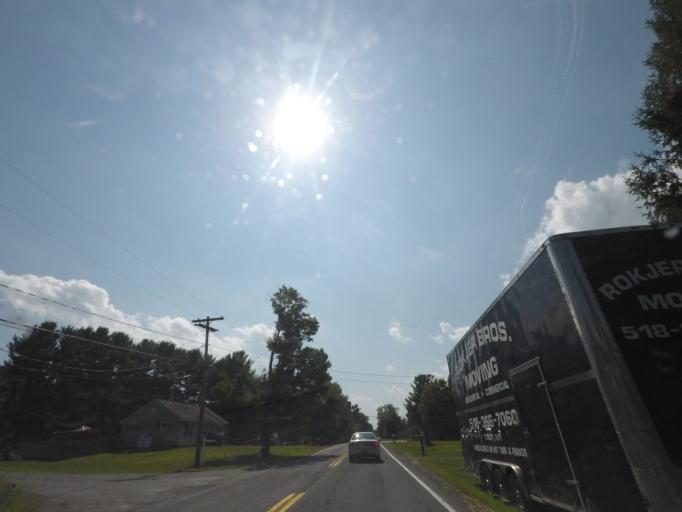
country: US
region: New York
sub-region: Rensselaer County
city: Poestenkill
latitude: 42.8131
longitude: -73.5065
